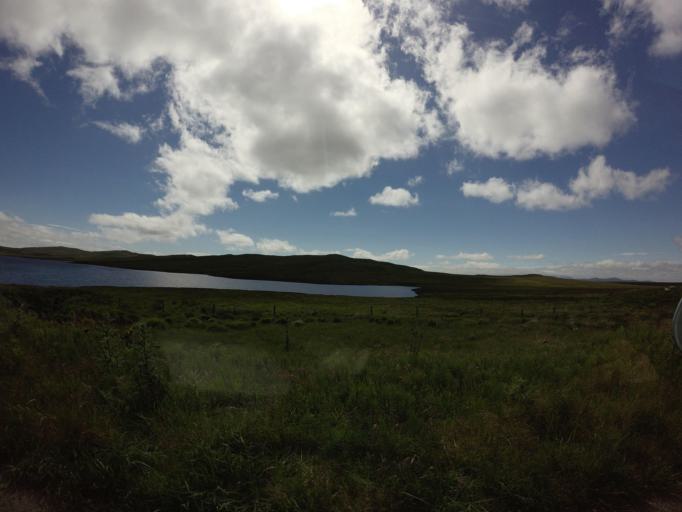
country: GB
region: Scotland
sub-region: Eilean Siar
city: Stornoway
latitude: 58.1611
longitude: -6.5347
